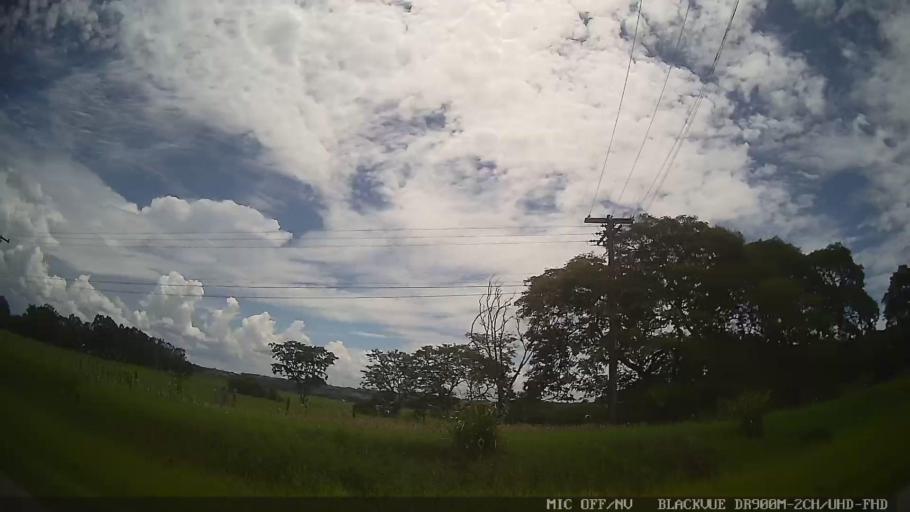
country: BR
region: Sao Paulo
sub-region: Conchas
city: Conchas
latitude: -23.0502
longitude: -47.9584
